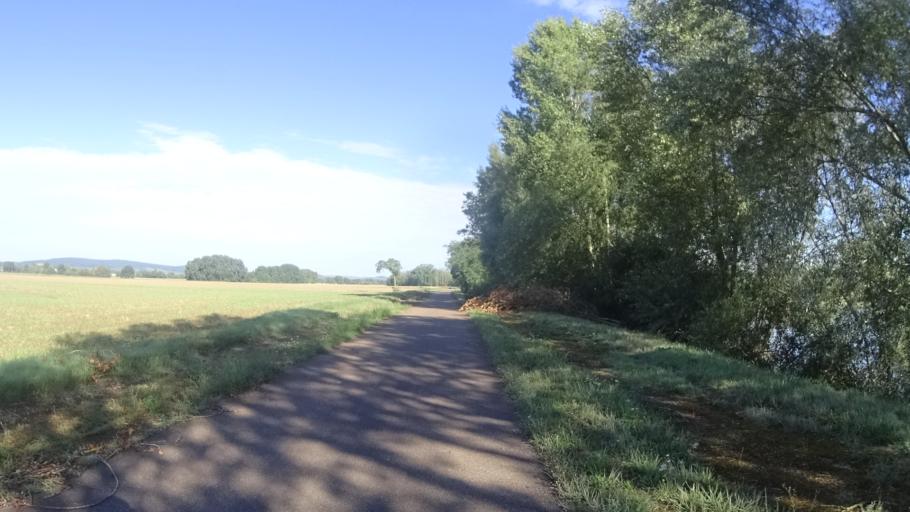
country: FR
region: Bourgogne
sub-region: Departement de la Nievre
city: Pouilly-sur-Loire
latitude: 47.2922
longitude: 2.9283
